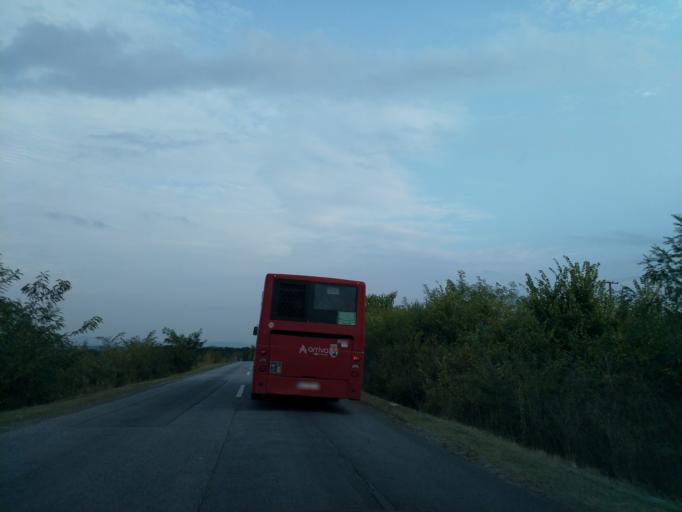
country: RS
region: Central Serbia
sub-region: Sumadijski Okrug
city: Kragujevac
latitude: 44.1303
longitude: 20.8143
